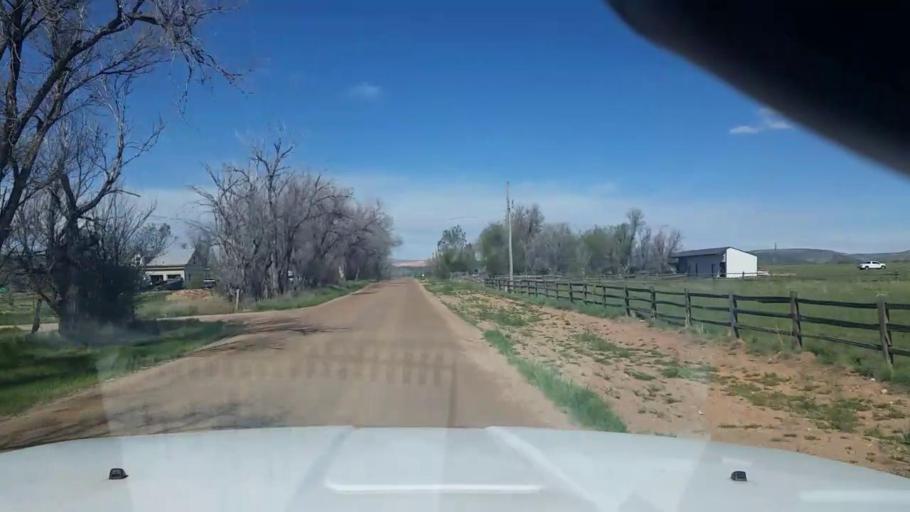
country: US
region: Colorado
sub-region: Larimer County
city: Wellington
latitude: 40.7839
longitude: -105.0893
